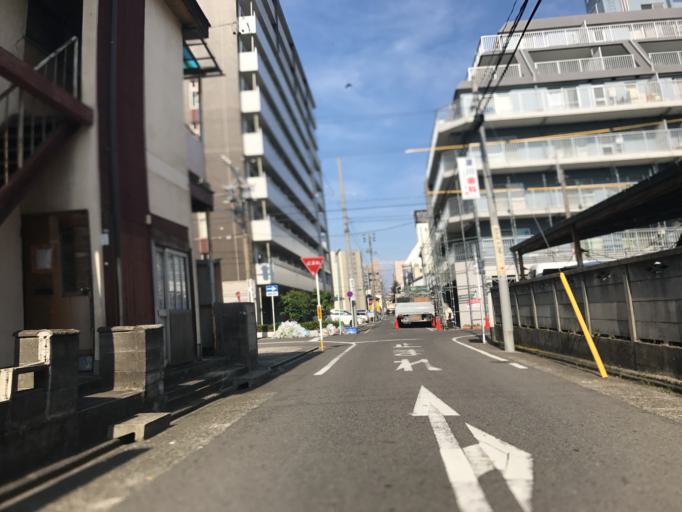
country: JP
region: Aichi
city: Nagoya-shi
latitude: 35.1658
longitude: 136.9404
